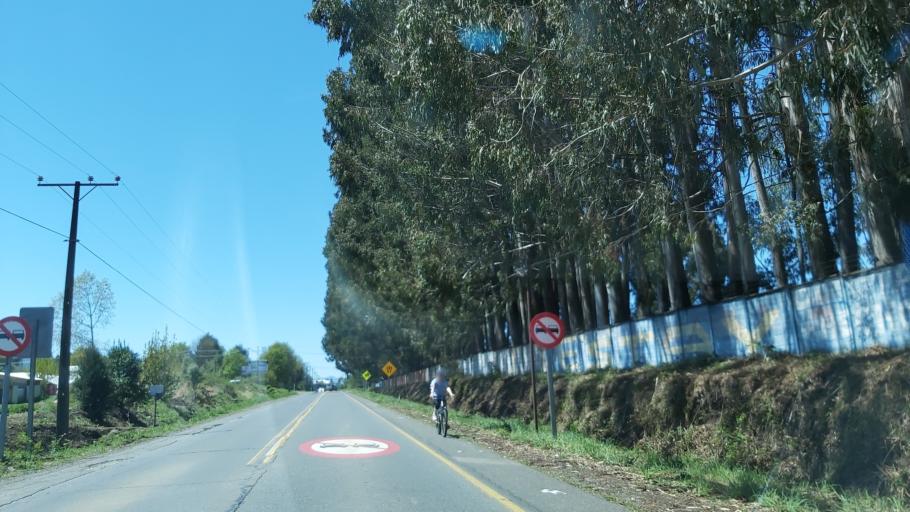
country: CL
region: Araucania
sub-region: Provincia de Cautin
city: Vilcun
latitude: -38.4341
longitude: -71.9047
